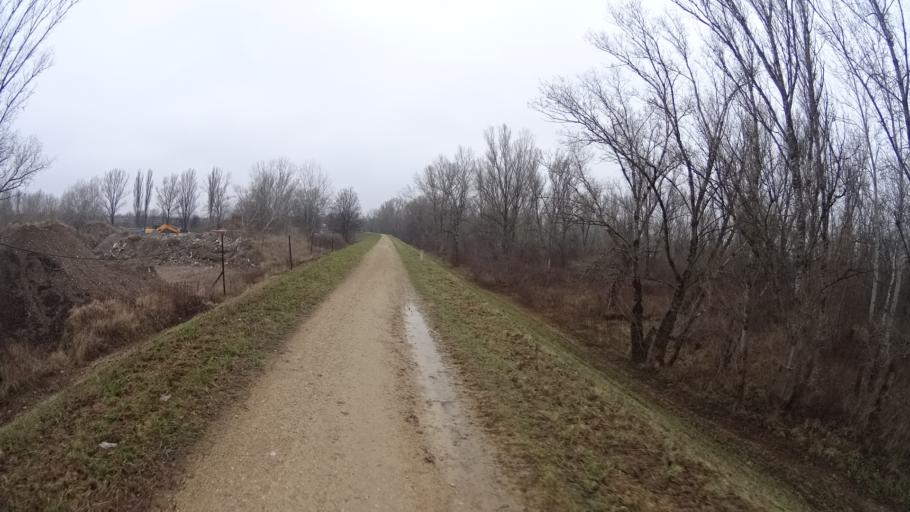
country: PL
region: Masovian Voivodeship
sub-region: Warszawa
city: Praga Poludnie
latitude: 52.2080
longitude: 21.0935
